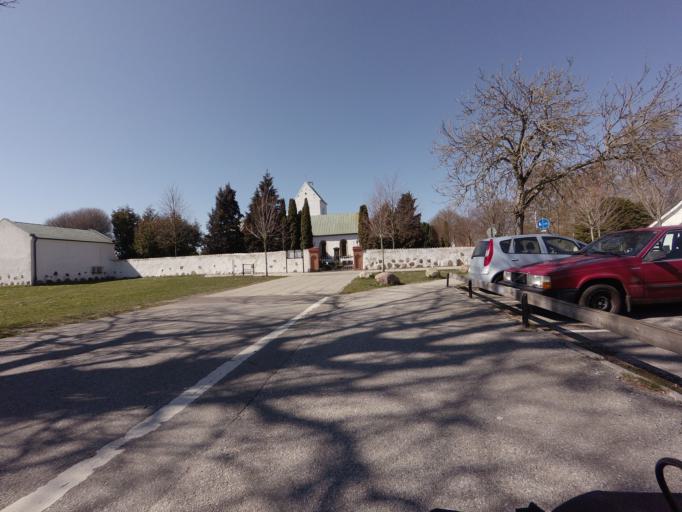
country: SE
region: Skane
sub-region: Vellinge Kommun
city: Vellinge
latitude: 55.4696
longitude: 13.0199
